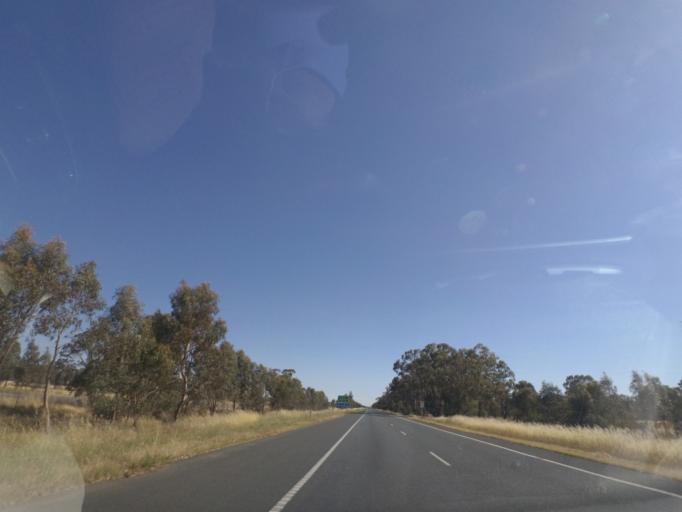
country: AU
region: Victoria
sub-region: Greater Shepparton
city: Shepparton
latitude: -36.7294
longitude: 145.1899
